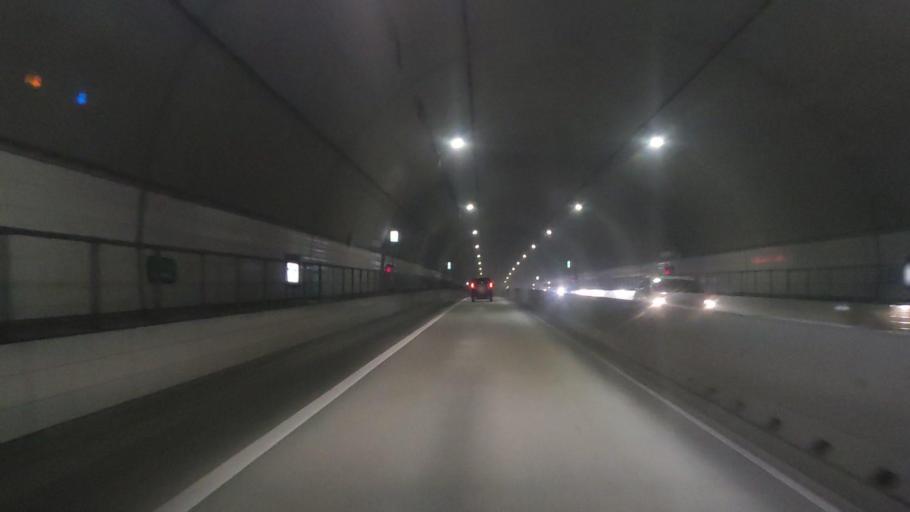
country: JP
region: Kumamoto
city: Ozu
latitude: 32.9096
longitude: 130.9675
